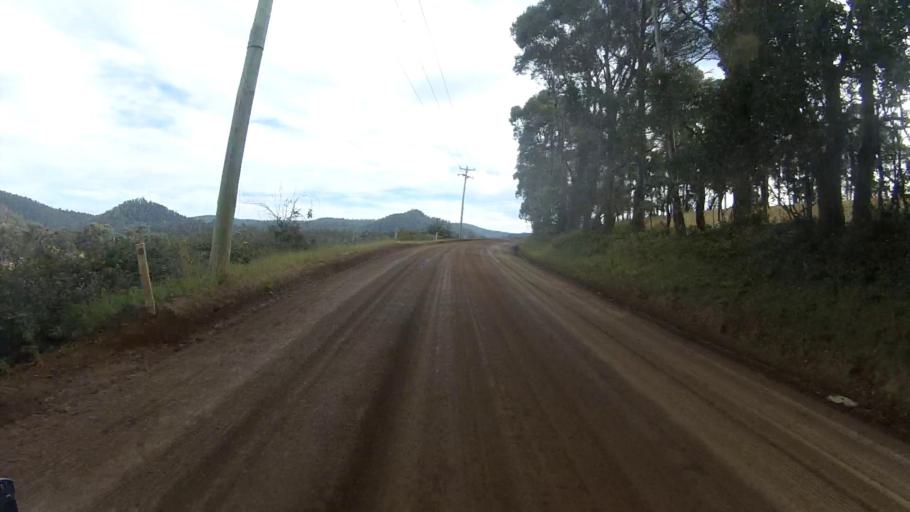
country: AU
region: Tasmania
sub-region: Sorell
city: Sorell
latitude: -42.7841
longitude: 147.8079
